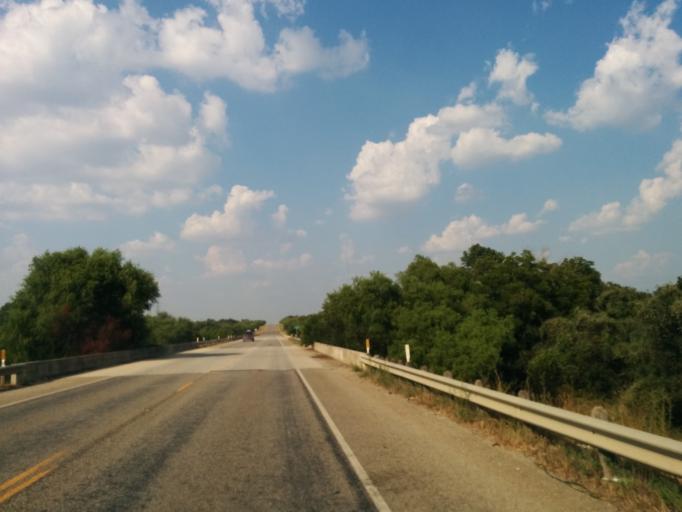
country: US
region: Texas
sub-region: Bexar County
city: Elmendorf
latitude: 29.2725
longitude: -98.3006
